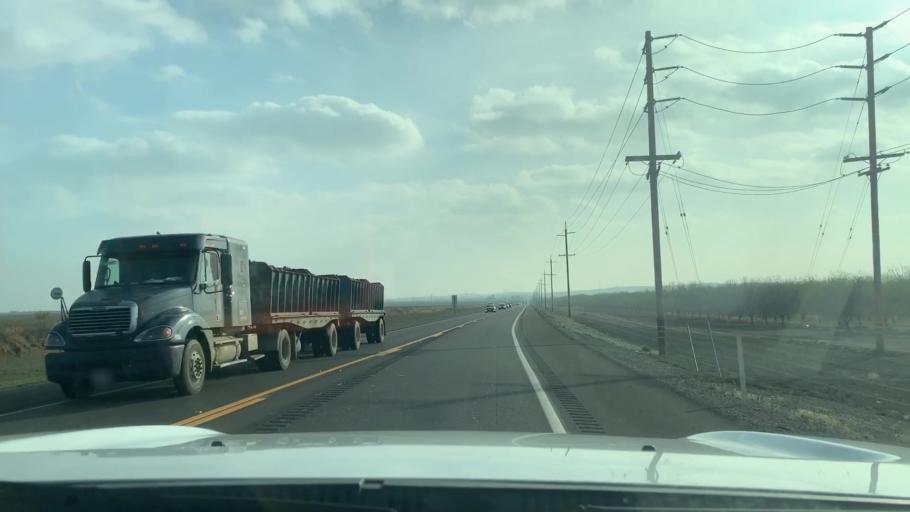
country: US
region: California
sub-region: Kings County
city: Kettleman City
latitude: 36.0342
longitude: -119.9591
